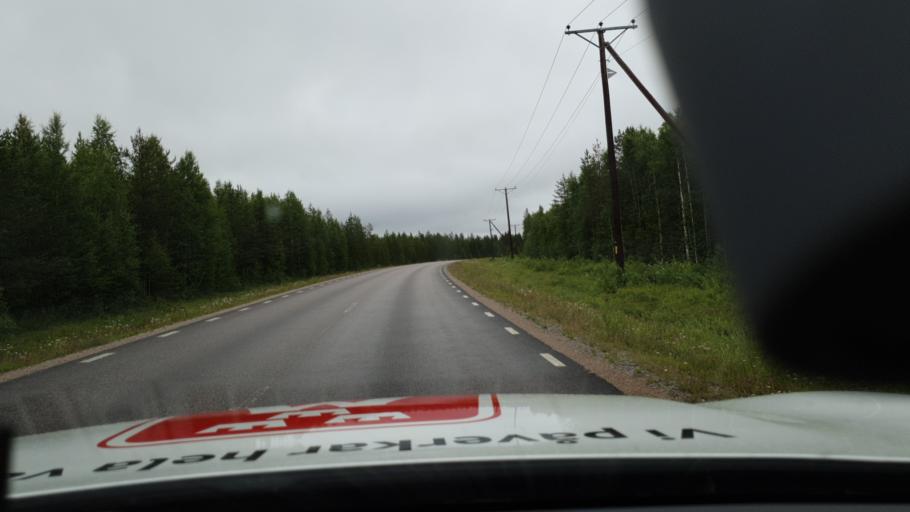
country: SE
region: Norrbotten
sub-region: Overtornea Kommun
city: OEvertornea
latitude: 66.3988
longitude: 23.5677
